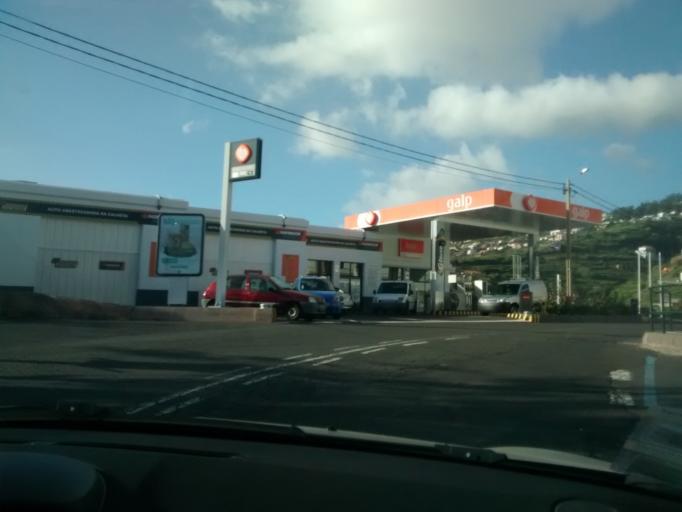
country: PT
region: Madeira
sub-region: Calheta
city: Estreito da Calheta
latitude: 32.7303
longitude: -17.1779
